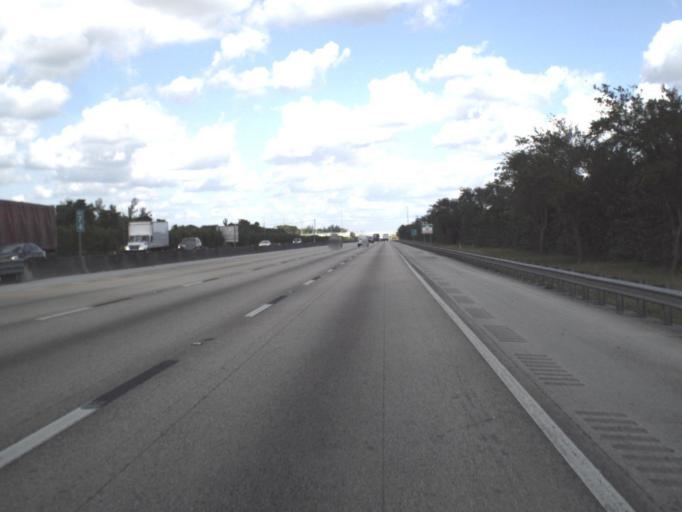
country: US
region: Florida
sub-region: Palm Beach County
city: Boca Pointe
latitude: 26.3396
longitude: -80.1703
